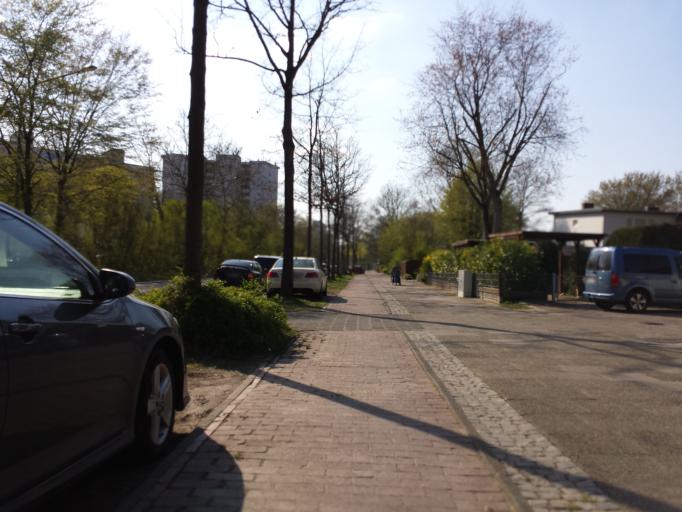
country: DE
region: Lower Saxony
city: Lilienthal
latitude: 53.0860
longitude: 8.8817
